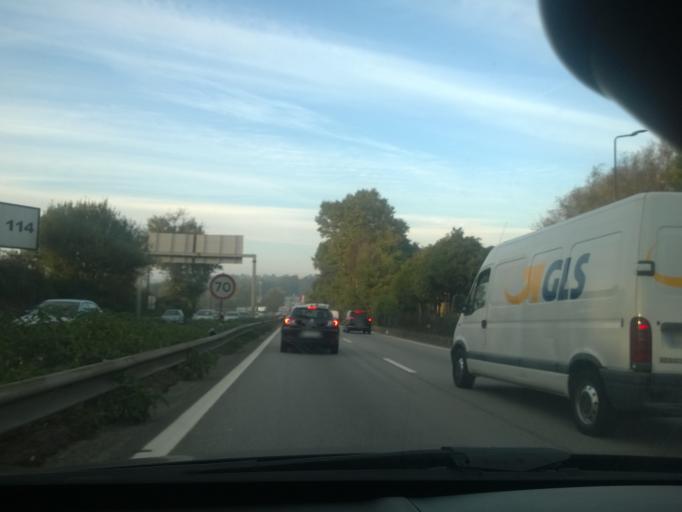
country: PT
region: Porto
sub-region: Maia
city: Leca do Bailio
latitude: 41.2131
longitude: -8.6271
